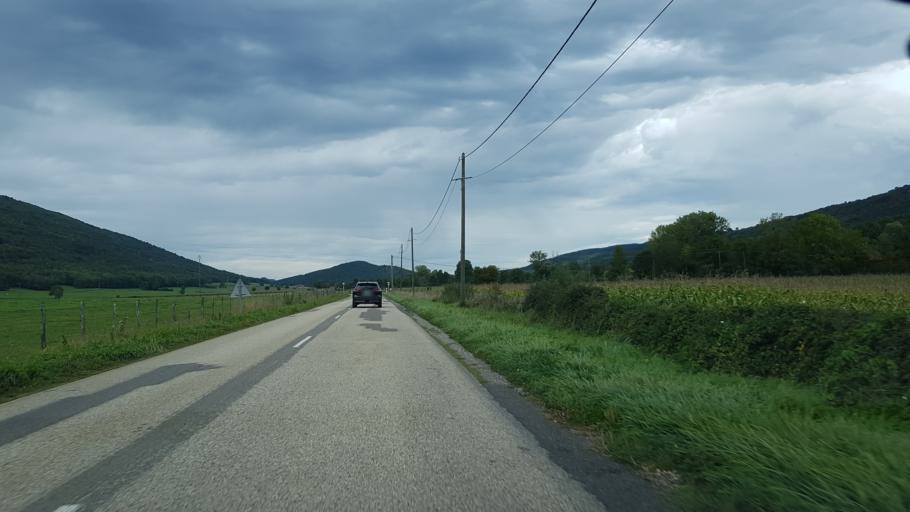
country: FR
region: Rhone-Alpes
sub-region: Departement de l'Ain
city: Cuisiat
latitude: 46.2801
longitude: 5.4306
